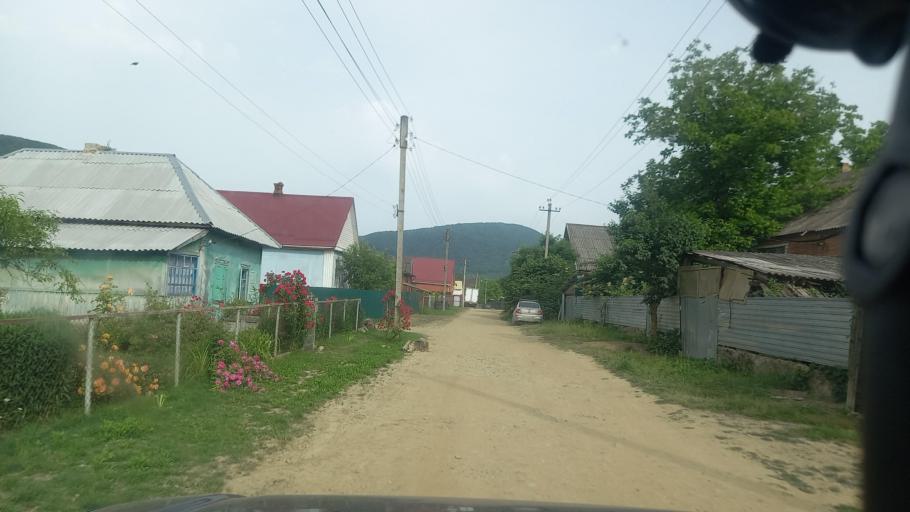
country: RU
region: Krasnodarskiy
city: Goryachiy Klyuch
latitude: 44.6054
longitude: 39.0272
